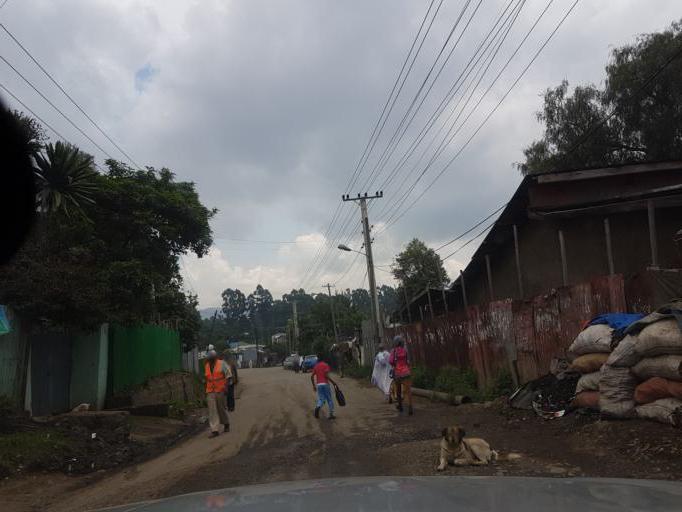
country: ET
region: Adis Abeba
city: Addis Ababa
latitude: 9.0237
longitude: 38.7680
